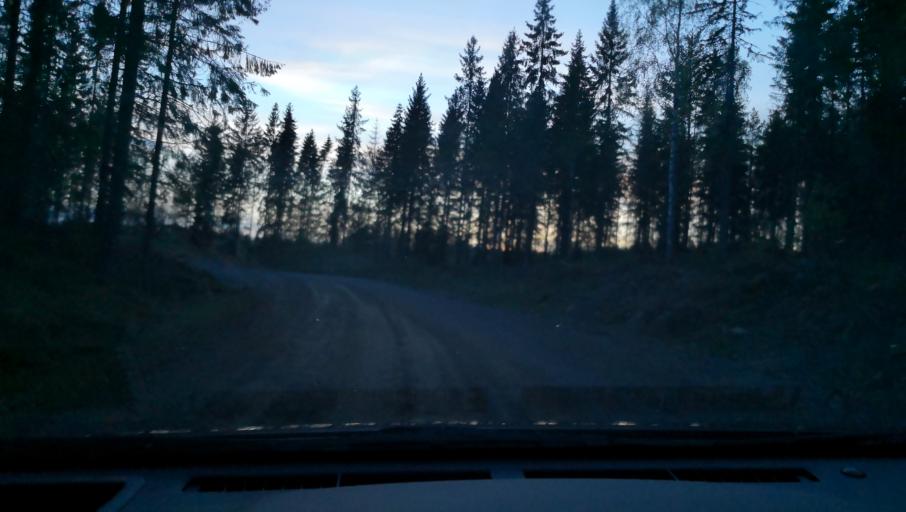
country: SE
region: OErebro
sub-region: Askersunds Kommun
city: Askersund
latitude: 58.9906
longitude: 14.9162
